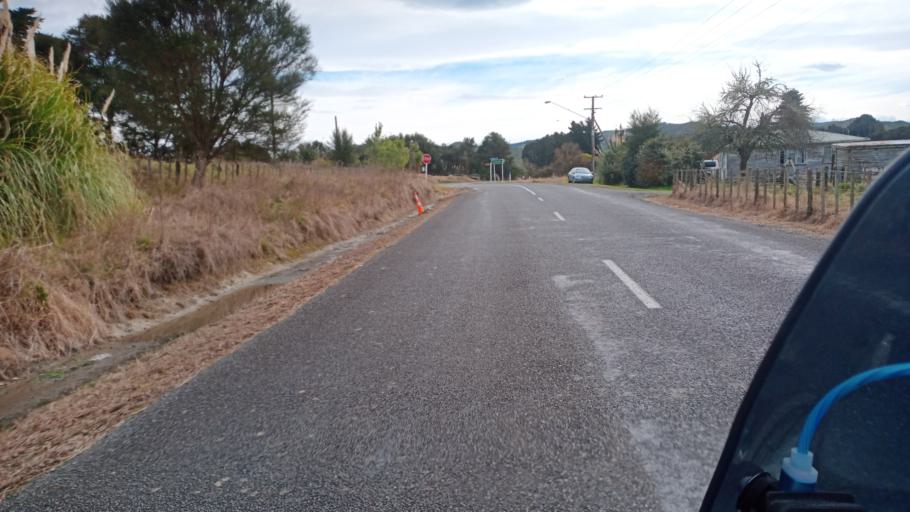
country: NZ
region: Hawke's Bay
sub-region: Wairoa District
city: Wairoa
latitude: -38.9730
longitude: 177.4150
